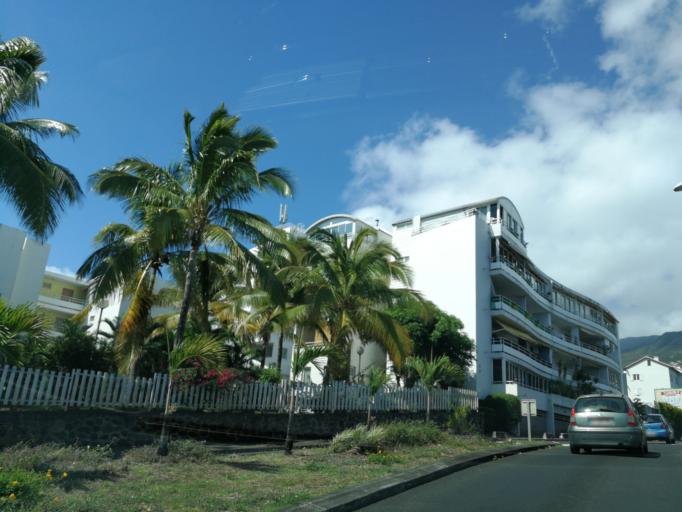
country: RE
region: Reunion
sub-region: Reunion
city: Saint-Denis
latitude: -20.9080
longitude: 55.4833
